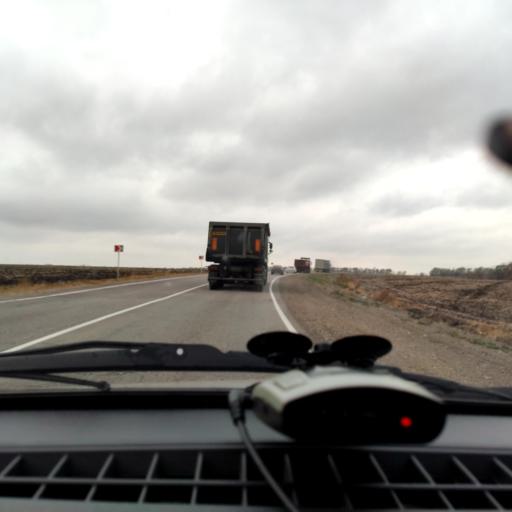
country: RU
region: Voronezj
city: Shilovo
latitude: 51.4526
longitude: 38.9763
